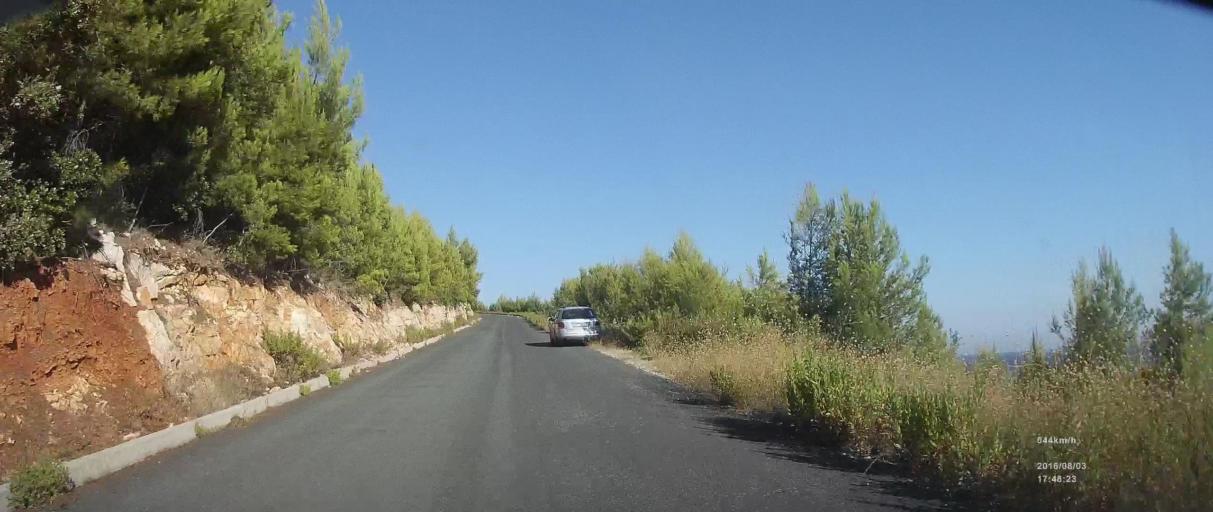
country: HR
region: Dubrovacko-Neretvanska
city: Blato
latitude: 42.7353
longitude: 17.5086
